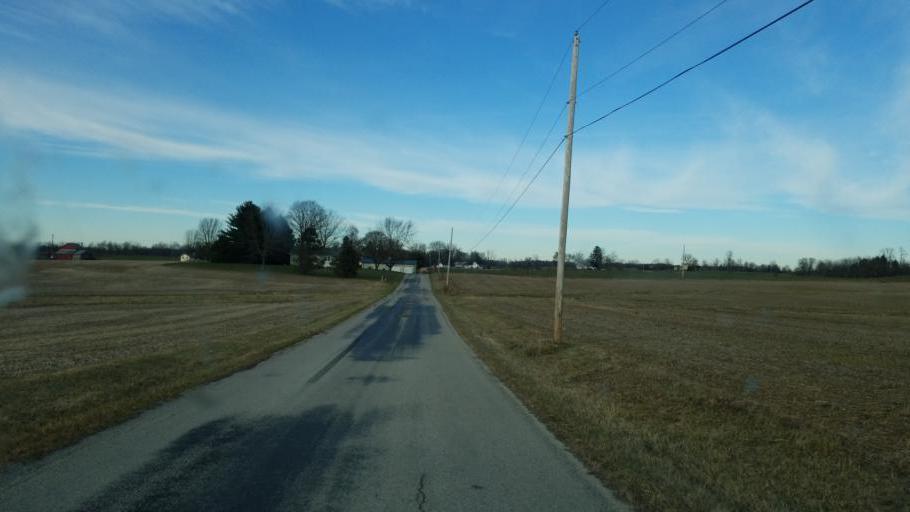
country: US
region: Ohio
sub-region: Morrow County
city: Mount Gilead
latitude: 40.5564
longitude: -82.7582
